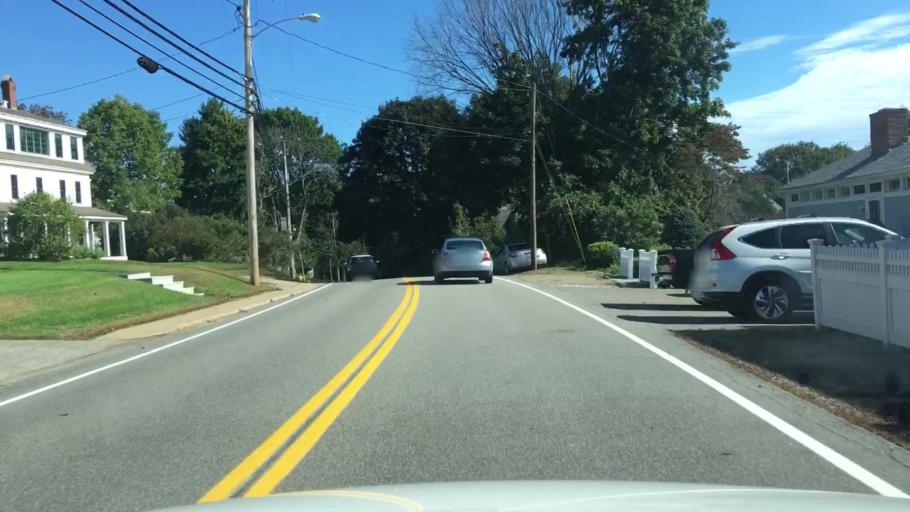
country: US
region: Maine
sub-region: York County
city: Kittery Point
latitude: 43.0839
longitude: -70.6989
